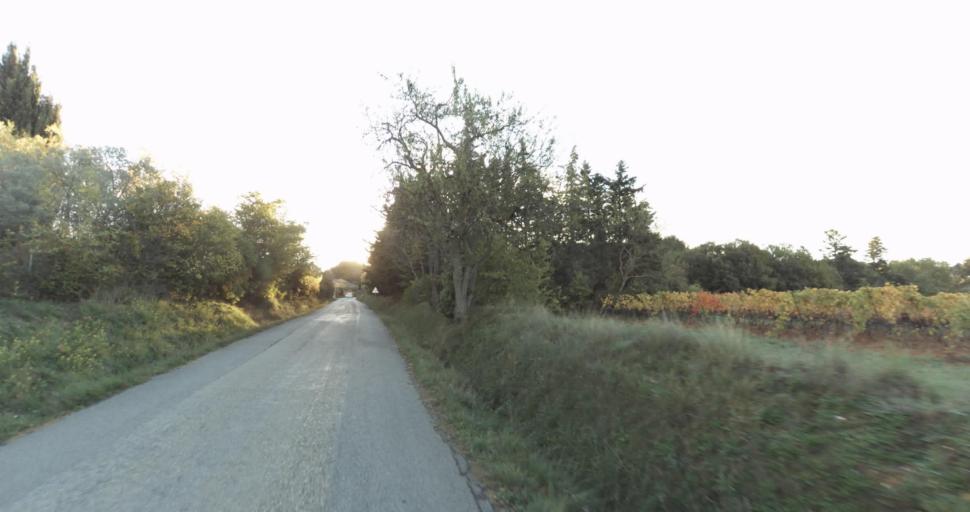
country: FR
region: Provence-Alpes-Cote d'Azur
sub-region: Departement des Bouches-du-Rhone
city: Venelles
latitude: 43.5771
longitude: 5.4828
